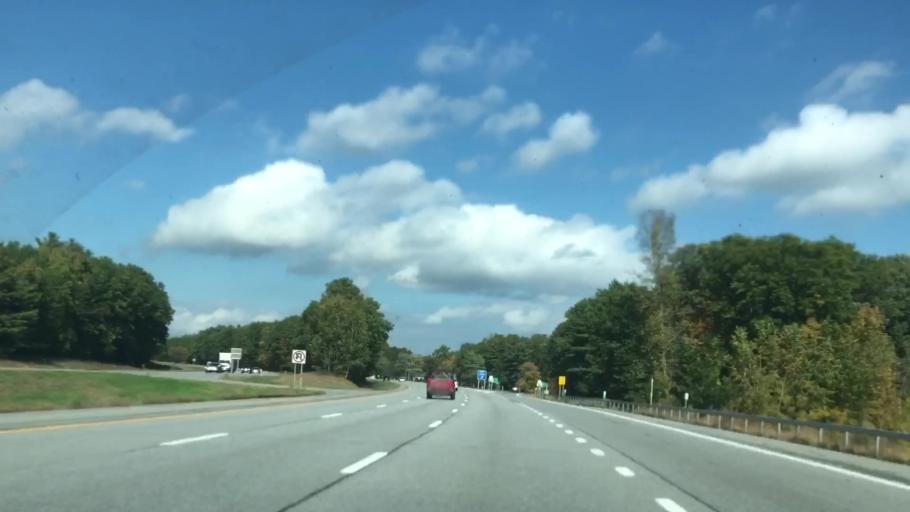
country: US
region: New York
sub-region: Warren County
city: West Glens Falls
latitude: 43.2684
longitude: -73.6742
